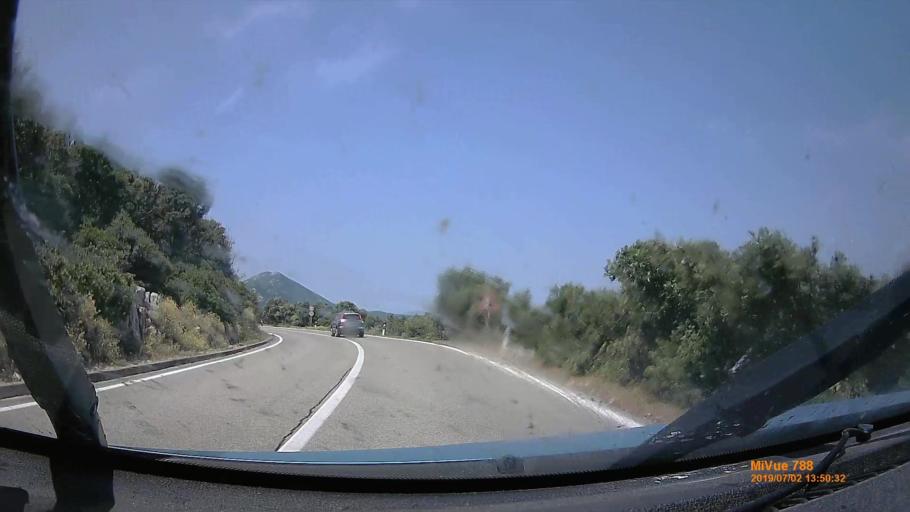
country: HR
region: Primorsko-Goranska
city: Mali Losinj
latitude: 44.5977
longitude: 14.4096
